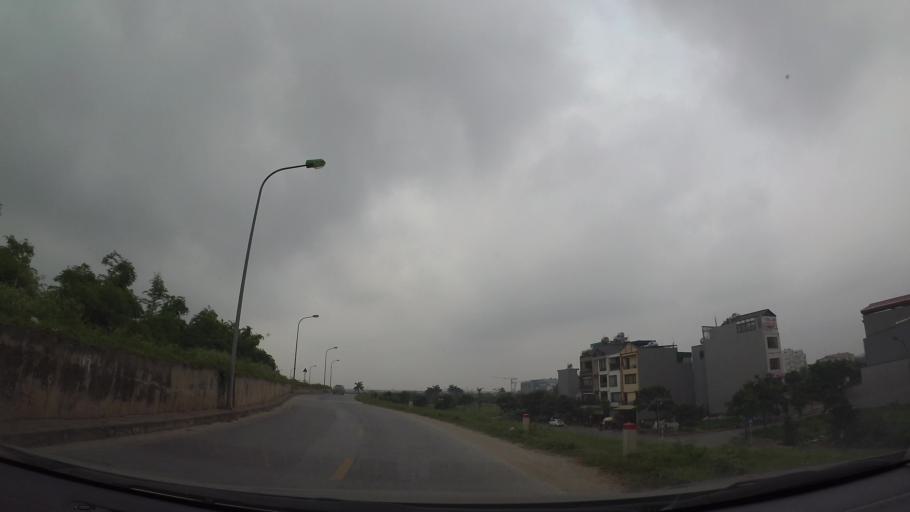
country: VN
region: Ha Noi
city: Trau Quy
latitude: 21.0577
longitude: 105.9185
